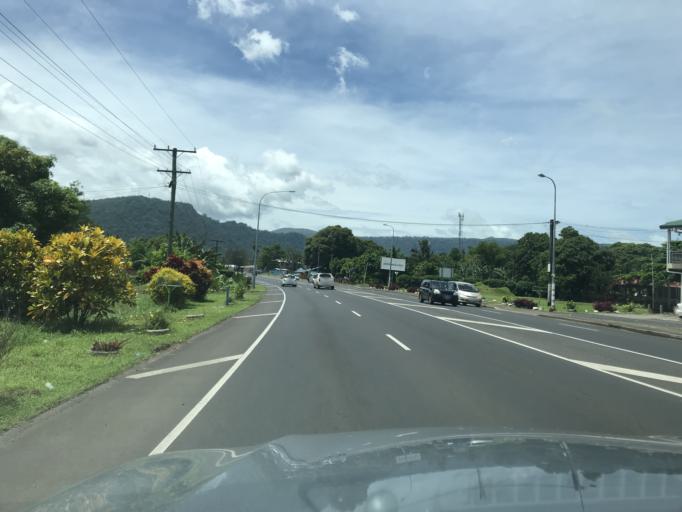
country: WS
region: Tuamasaga
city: Vaiusu
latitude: -13.8305
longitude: -171.7917
